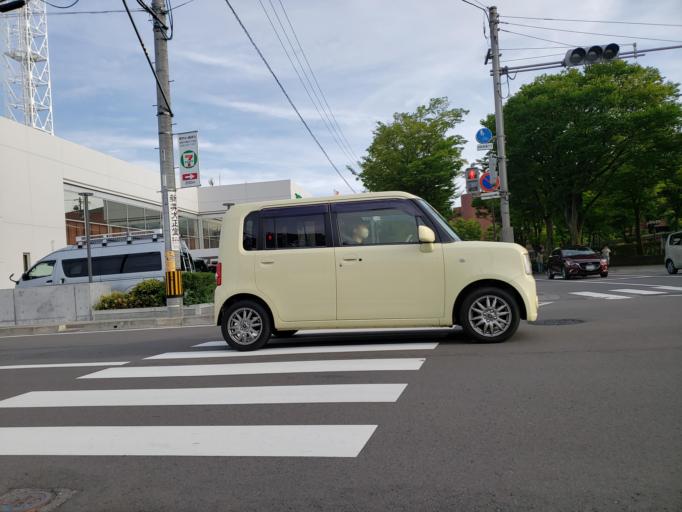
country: JP
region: Nagano
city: Nagano-shi
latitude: 36.6372
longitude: 138.1876
